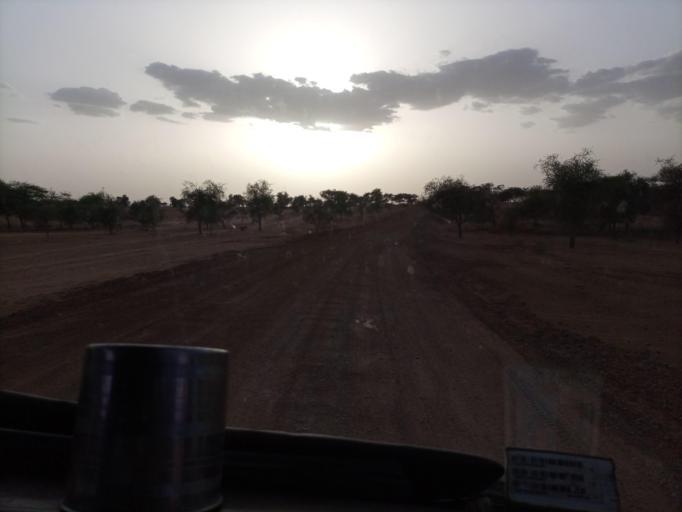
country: SN
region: Louga
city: Dara
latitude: 15.3735
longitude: -15.5849
